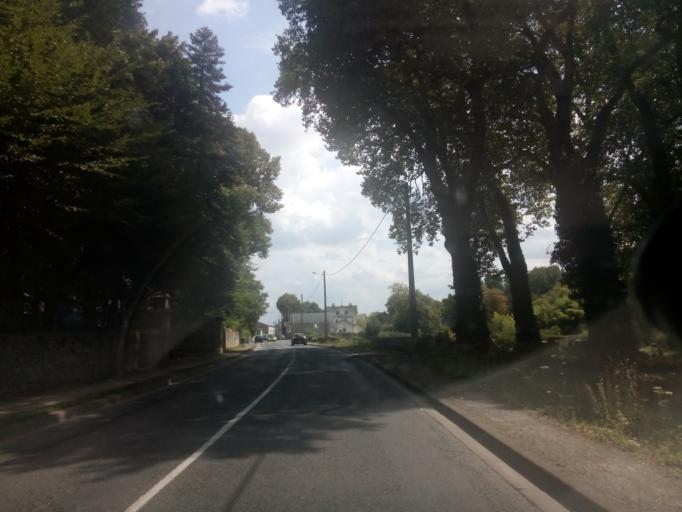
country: FR
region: Centre
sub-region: Departement d'Indre-et-Loire
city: Azay-le-Rideau
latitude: 47.2647
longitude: 0.4485
